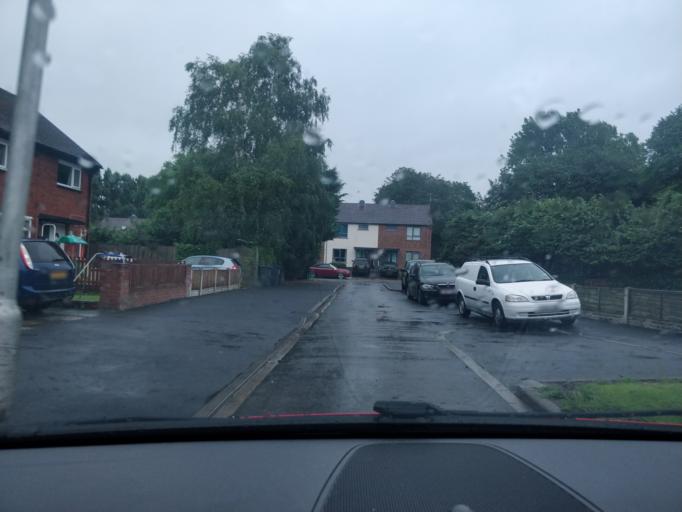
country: GB
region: England
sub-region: Lancashire
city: Banks
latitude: 53.6786
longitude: -2.9185
